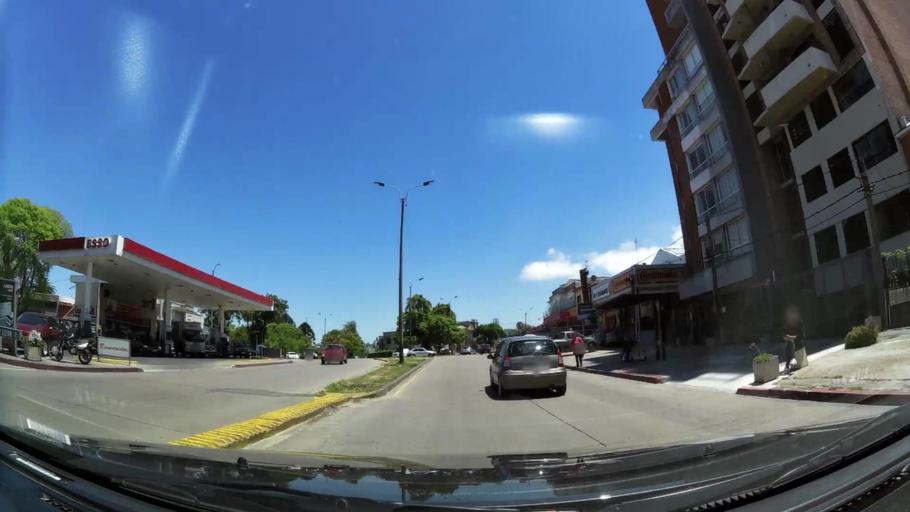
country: UY
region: Montevideo
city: Montevideo
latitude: -34.8960
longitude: -56.1467
